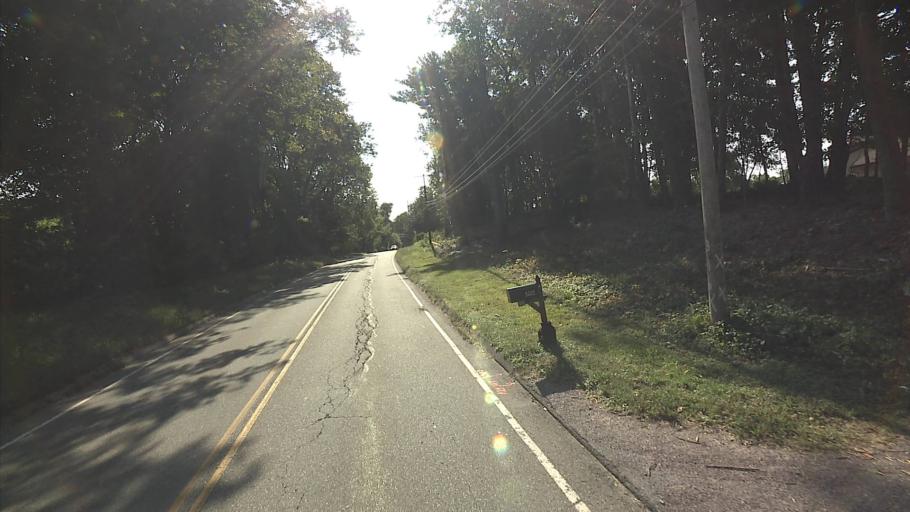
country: US
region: Connecticut
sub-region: Windham County
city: South Windham
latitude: 41.6307
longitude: -72.2040
